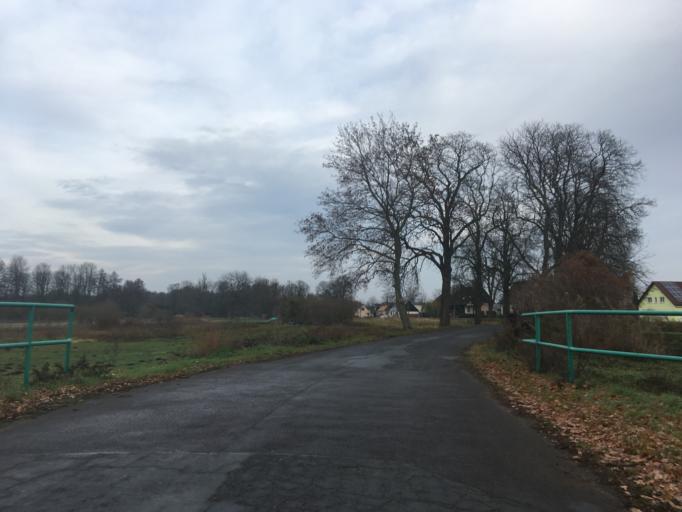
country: DE
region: Brandenburg
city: Seelow
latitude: 52.5661
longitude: 14.3473
